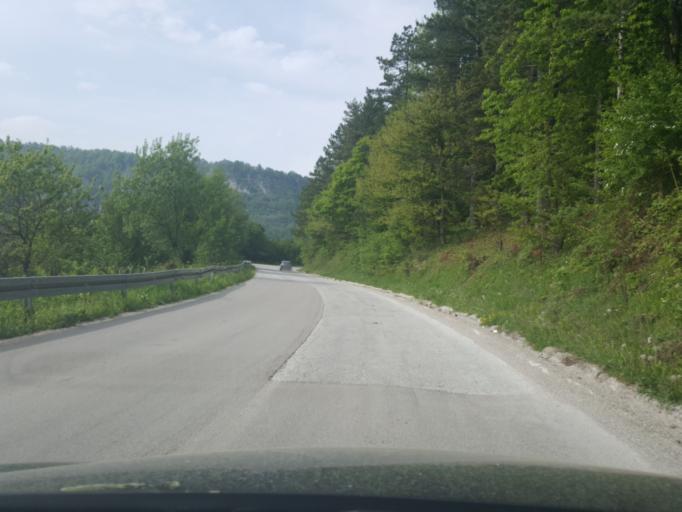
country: RS
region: Central Serbia
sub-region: Zlatiborski Okrug
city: Bajina Basta
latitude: 44.0834
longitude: 19.6582
